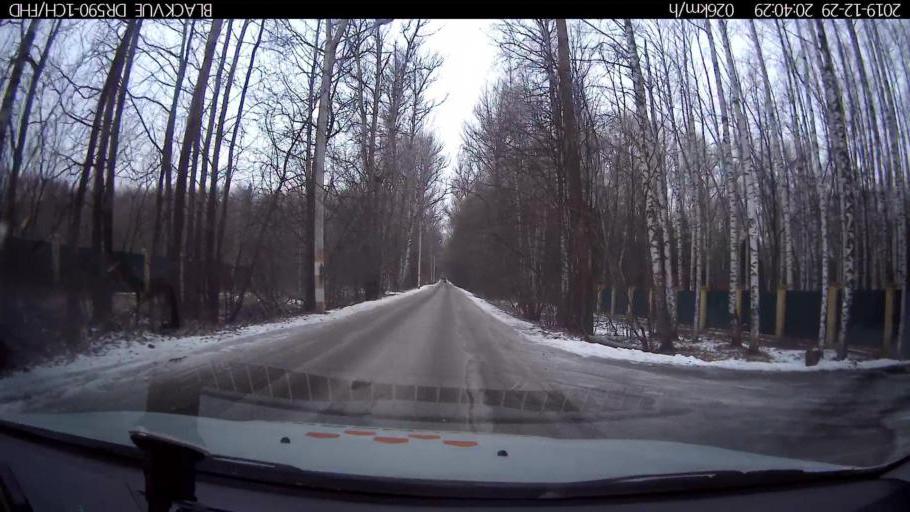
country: RU
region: Nizjnij Novgorod
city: Afonino
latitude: 56.1899
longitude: 44.0436
